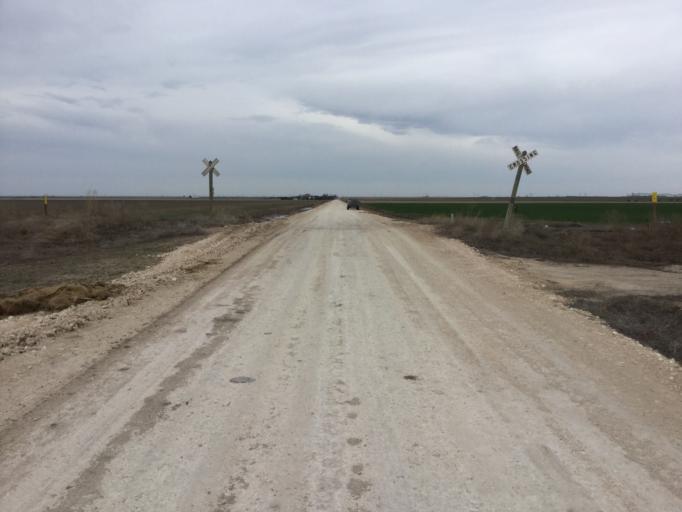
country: US
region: Kansas
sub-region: Scott County
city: Scott City
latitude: 38.4534
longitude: -100.9130
